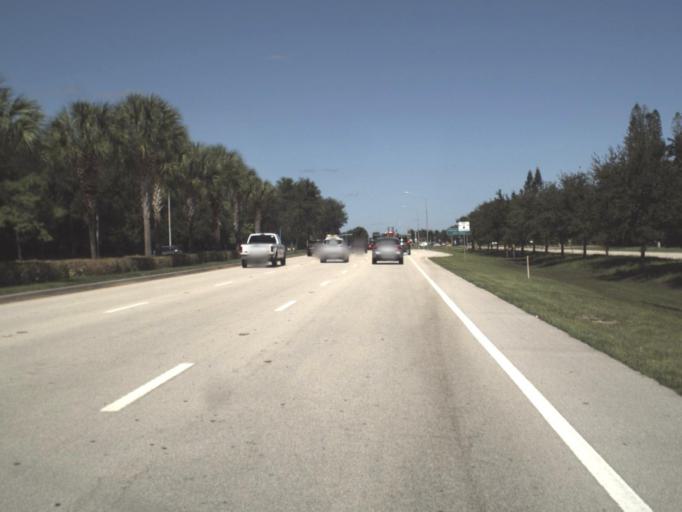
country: US
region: Florida
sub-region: Collier County
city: Pelican Bay
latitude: 26.2405
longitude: -81.8009
